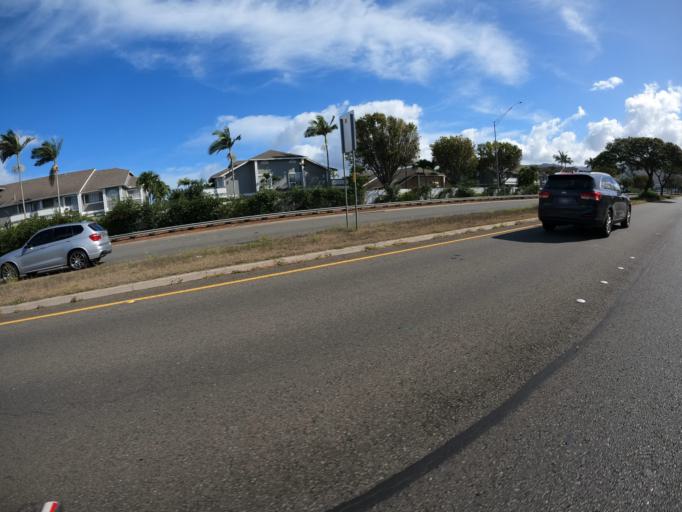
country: US
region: Hawaii
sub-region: Honolulu County
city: Halawa
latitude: 21.3682
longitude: -157.9233
